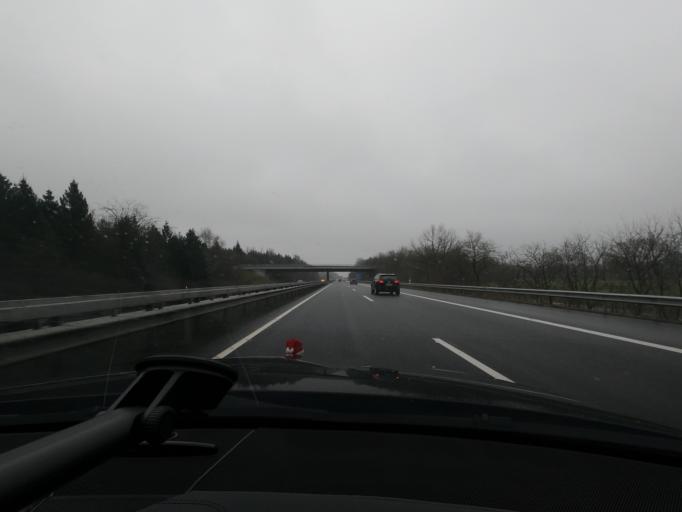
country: DE
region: Schleswig-Holstein
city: Gross Vollstedt
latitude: 54.2259
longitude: 9.8436
